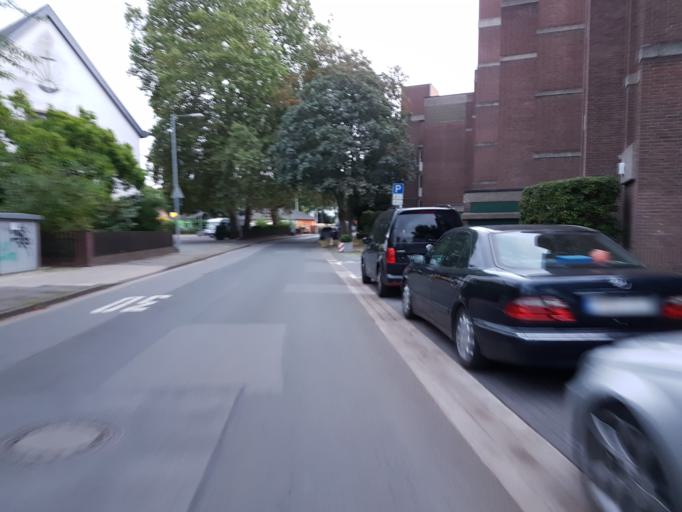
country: DE
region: Lower Saxony
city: Hannover
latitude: 52.3964
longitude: 9.7528
